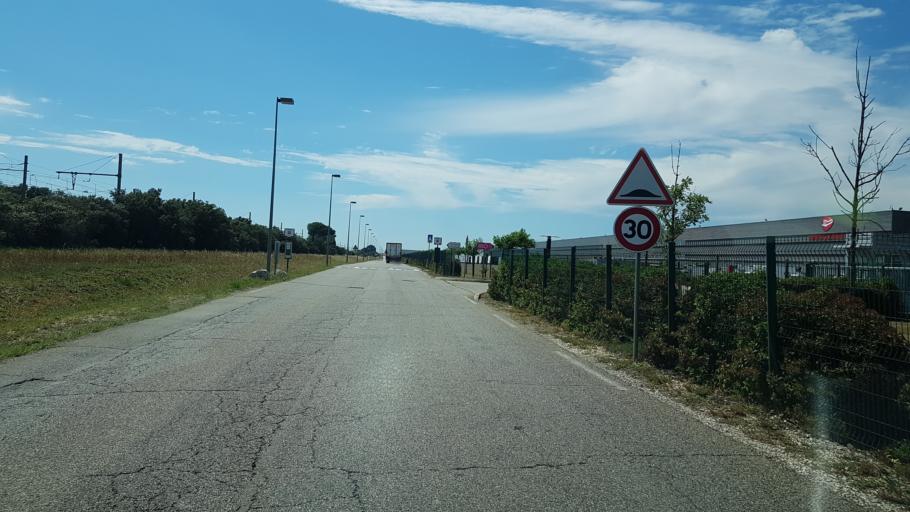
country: FR
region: Provence-Alpes-Cote d'Azur
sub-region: Departement des Bouches-du-Rhone
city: Saint-Martin-de-Crau
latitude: 43.6248
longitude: 4.7906
